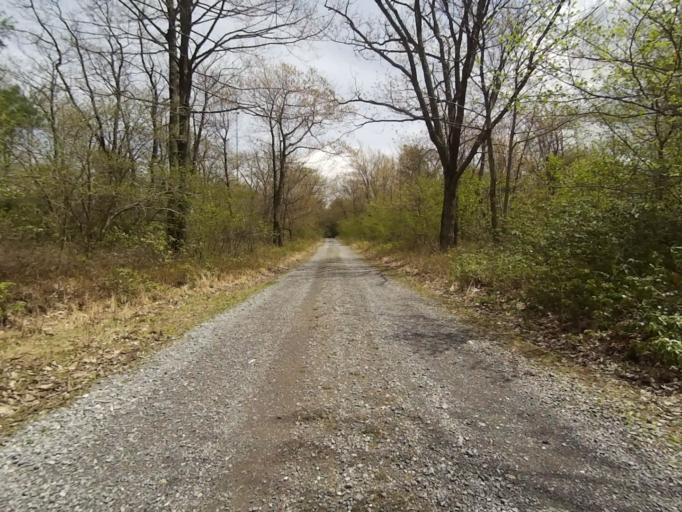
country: US
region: Pennsylvania
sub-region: Centre County
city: Boalsburg
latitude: 40.7524
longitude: -77.7584
